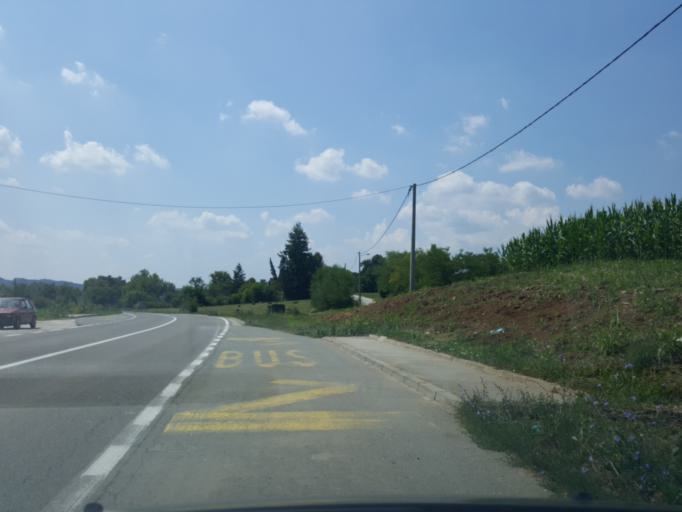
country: RS
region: Central Serbia
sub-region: Sumadijski Okrug
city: Topola
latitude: 44.3106
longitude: 20.6978
